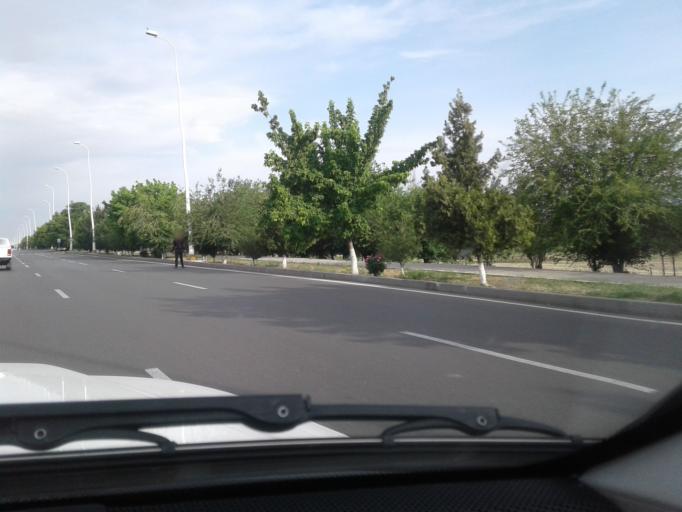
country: TM
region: Ahal
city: Abadan
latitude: 38.0149
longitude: 58.2652
